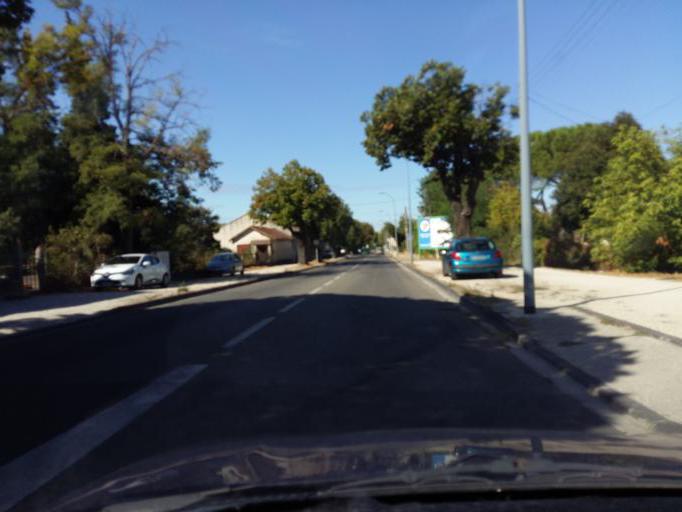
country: FR
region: Provence-Alpes-Cote d'Azur
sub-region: Departement du Vaucluse
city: Carpentras
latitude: 44.0570
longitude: 5.0622
